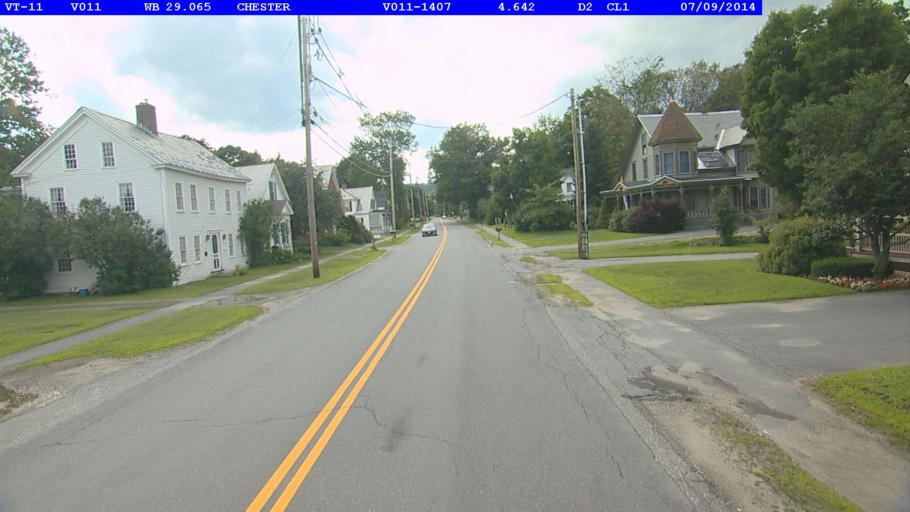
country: US
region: Vermont
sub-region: Windsor County
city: Chester
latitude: 43.2659
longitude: -72.6032
